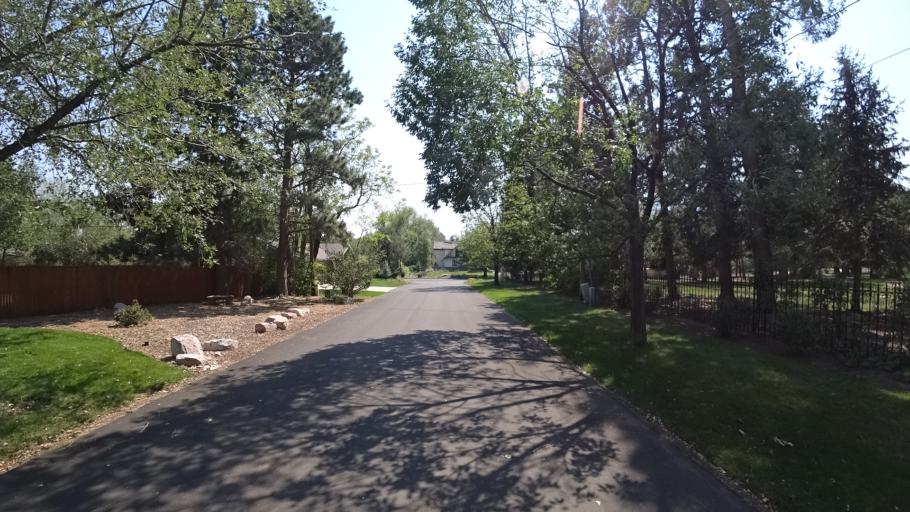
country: US
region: Colorado
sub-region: El Paso County
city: Colorado Springs
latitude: 38.7976
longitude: -104.8420
